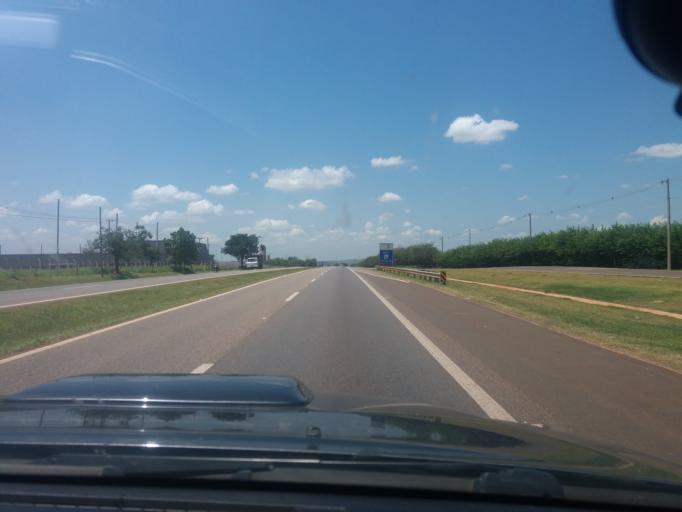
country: BR
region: Sao Paulo
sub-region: Tatui
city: Tatui
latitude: -23.3489
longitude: -47.8786
